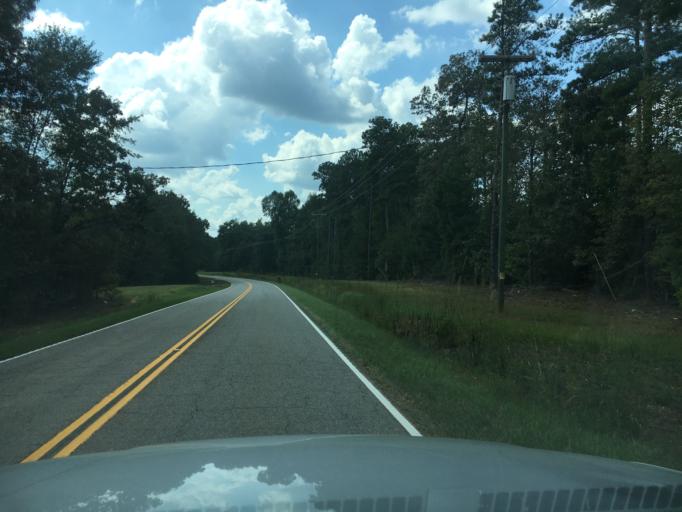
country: US
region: South Carolina
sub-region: Greenwood County
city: Greenwood
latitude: 34.0785
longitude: -82.1421
